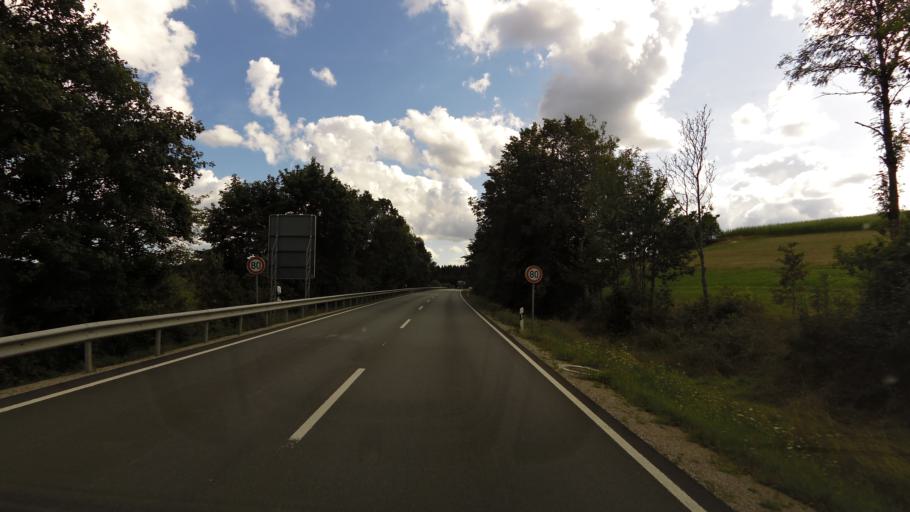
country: DE
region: Bavaria
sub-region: Lower Bavaria
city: Loitzendorf
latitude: 49.1161
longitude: 12.6506
